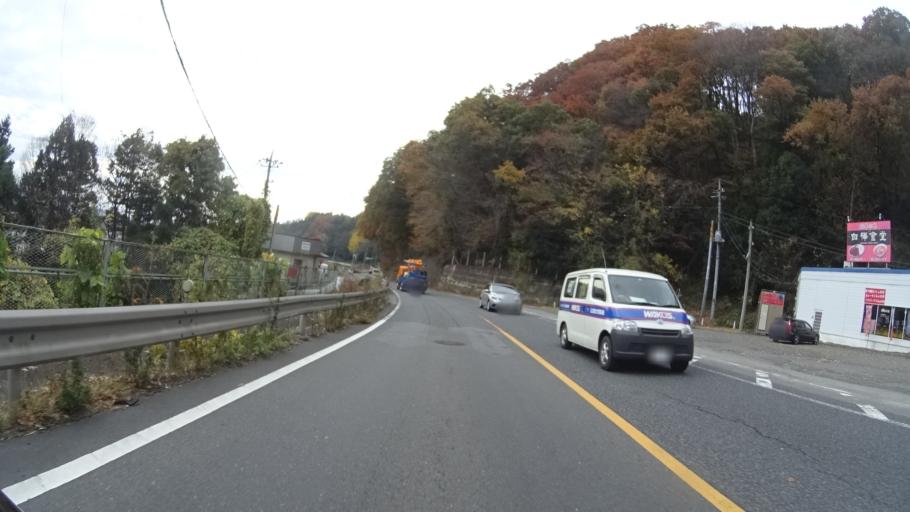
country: JP
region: Gunma
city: Shibukawa
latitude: 36.5538
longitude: 139.0315
